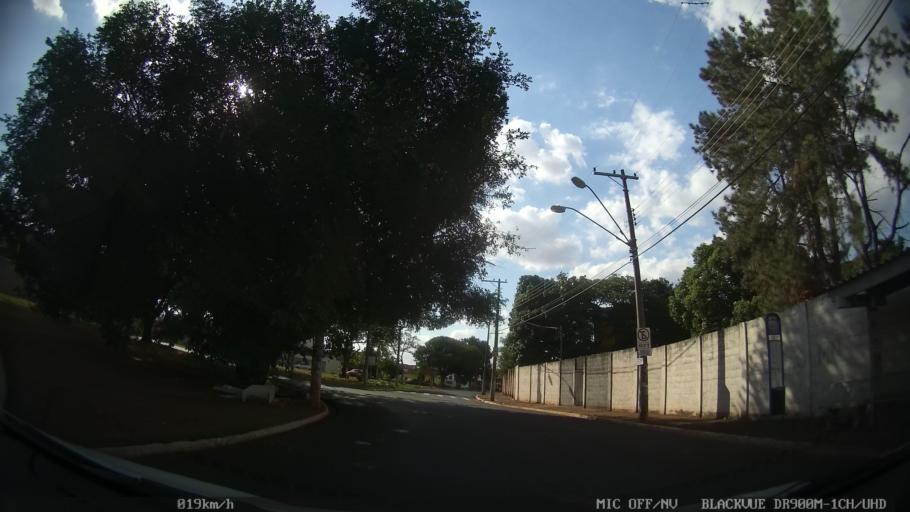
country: BR
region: Sao Paulo
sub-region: Ribeirao Preto
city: Ribeirao Preto
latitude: -21.1895
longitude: -47.8259
